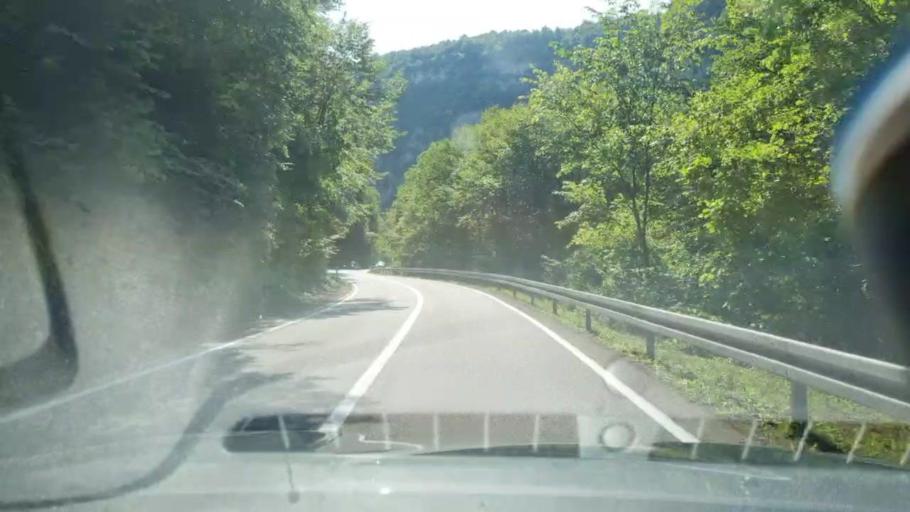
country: BA
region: Federation of Bosnia and Herzegovina
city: Bosanska Krupa
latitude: 44.8696
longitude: 16.1008
